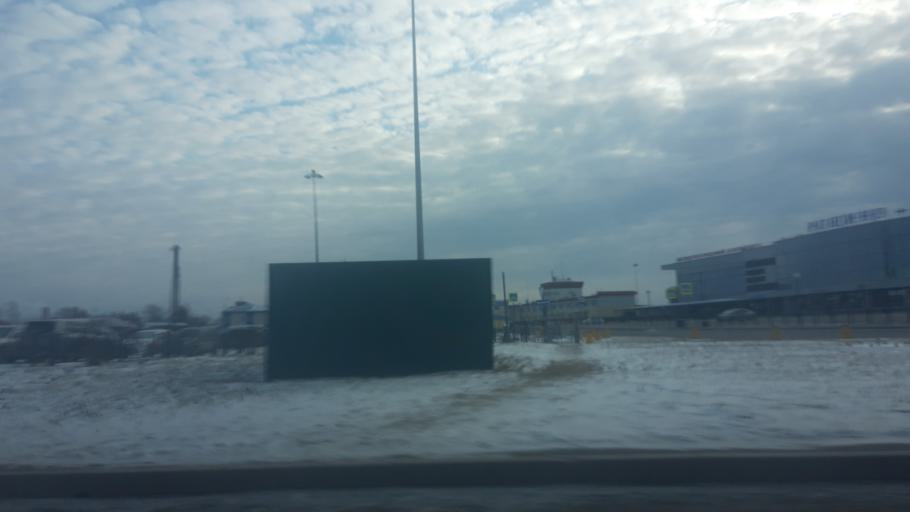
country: RU
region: Tjumen
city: Moskovskiy
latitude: 57.1828
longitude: 65.3492
